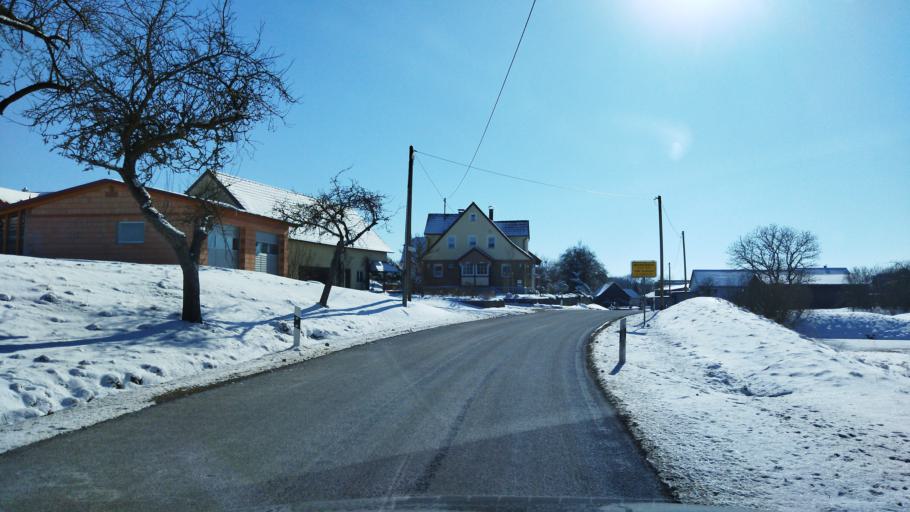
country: DE
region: Baden-Wuerttemberg
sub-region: Regierungsbezirk Stuttgart
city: Langenburg
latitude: 49.2519
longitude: 9.8922
